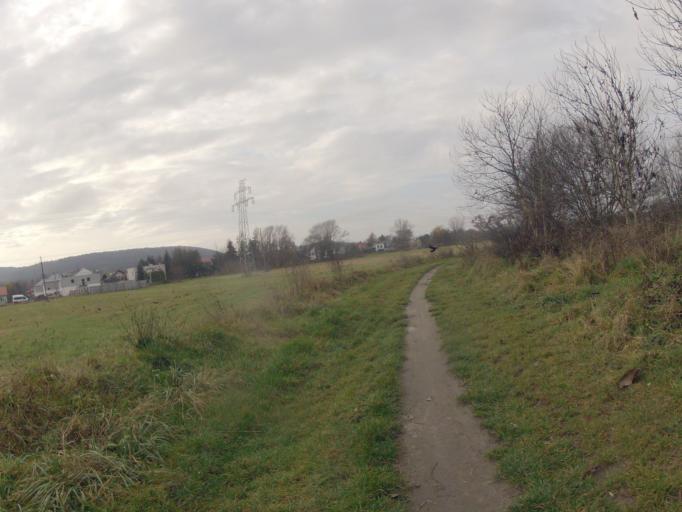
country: PL
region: Lesser Poland Voivodeship
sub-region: Powiat krakowski
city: Rzaska
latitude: 50.0764
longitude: 19.8662
